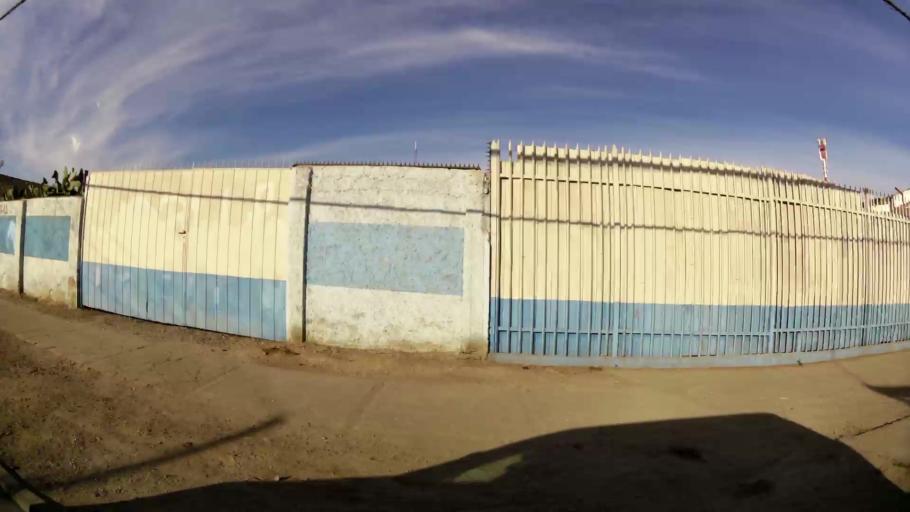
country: CL
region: Santiago Metropolitan
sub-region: Provincia de Cordillera
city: Puente Alto
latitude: -33.6114
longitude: -70.5787
